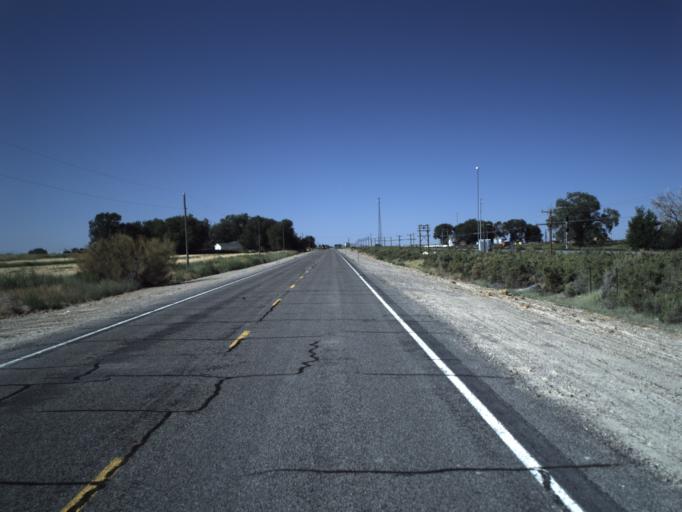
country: US
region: Utah
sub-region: Millard County
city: Delta
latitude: 39.5438
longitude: -112.3609
